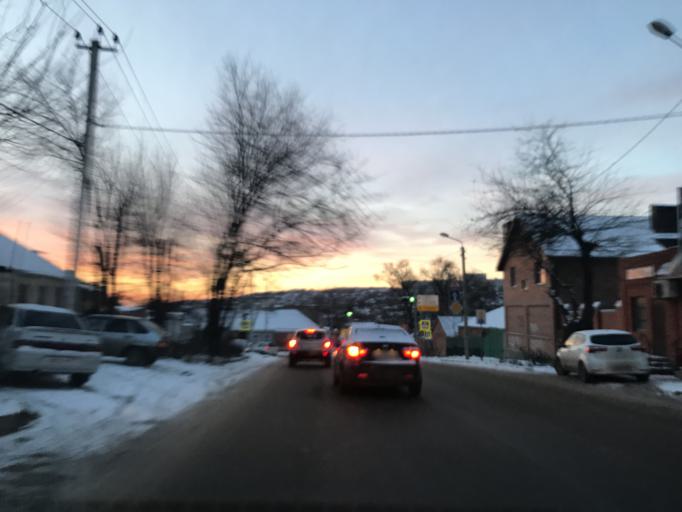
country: RU
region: Rostov
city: Rostov-na-Donu
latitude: 47.2273
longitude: 39.6816
